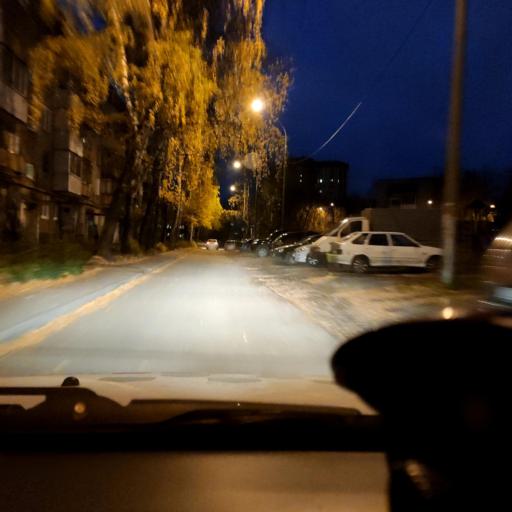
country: RU
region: Perm
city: Perm
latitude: 57.9612
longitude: 56.2253
